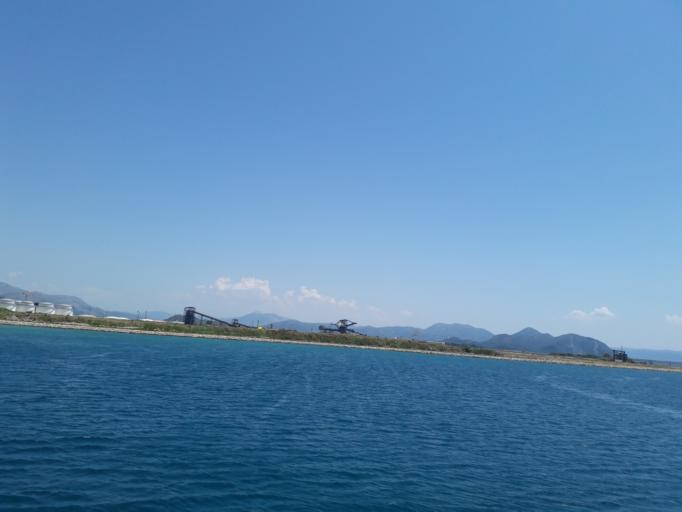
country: HR
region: Dubrovacko-Neretvanska
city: Komin
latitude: 43.0380
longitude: 17.4174
